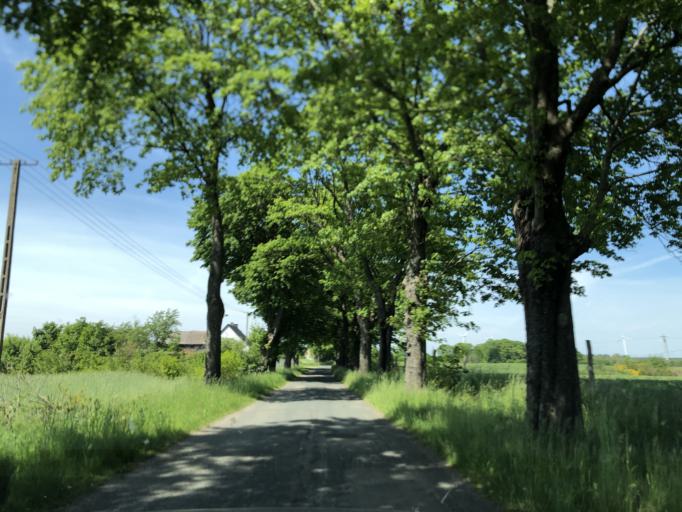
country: PL
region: West Pomeranian Voivodeship
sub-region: Powiat kolobrzeski
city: Goscino
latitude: 54.0387
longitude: 15.7295
